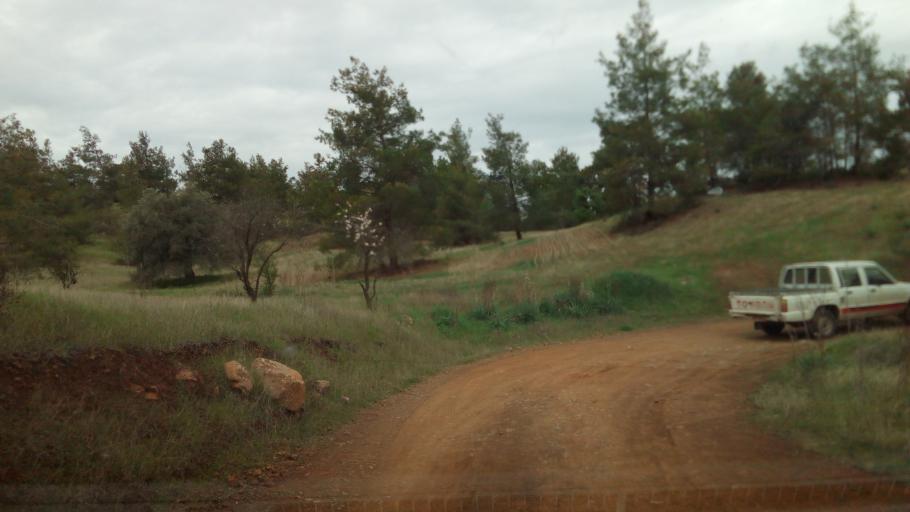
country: CY
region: Lefkosia
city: Klirou
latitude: 35.0001
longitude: 33.1057
